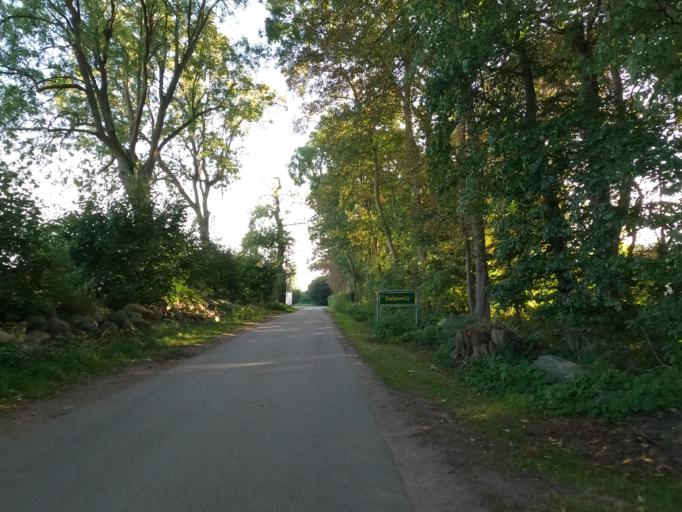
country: DE
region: Schleswig-Holstein
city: Neukirchen
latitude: 54.3159
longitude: 11.0229
